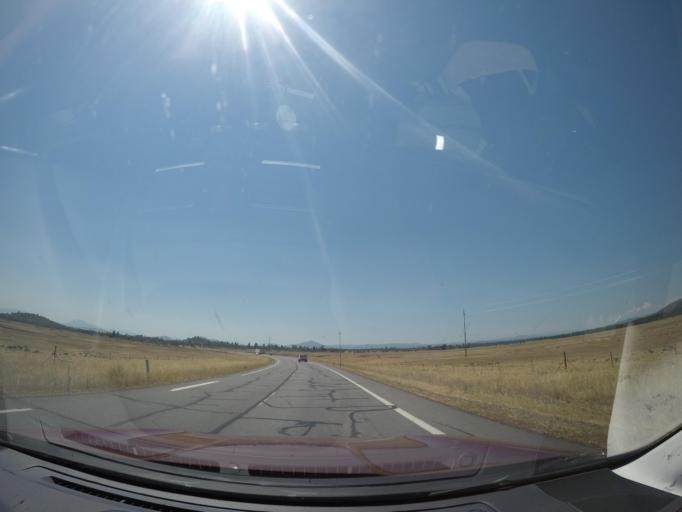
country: US
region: California
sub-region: Shasta County
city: Burney
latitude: 41.0994
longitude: -121.2932
